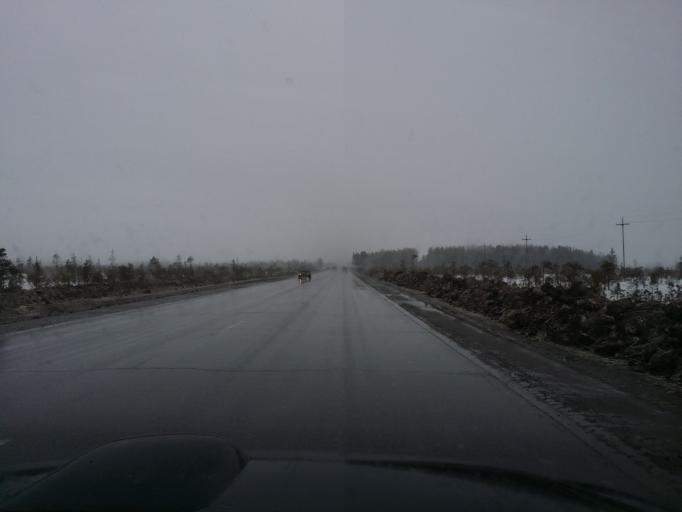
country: RU
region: Khanty-Mansiyskiy Avtonomnyy Okrug
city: Nizhnevartovsk
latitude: 60.9589
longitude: 76.7348
